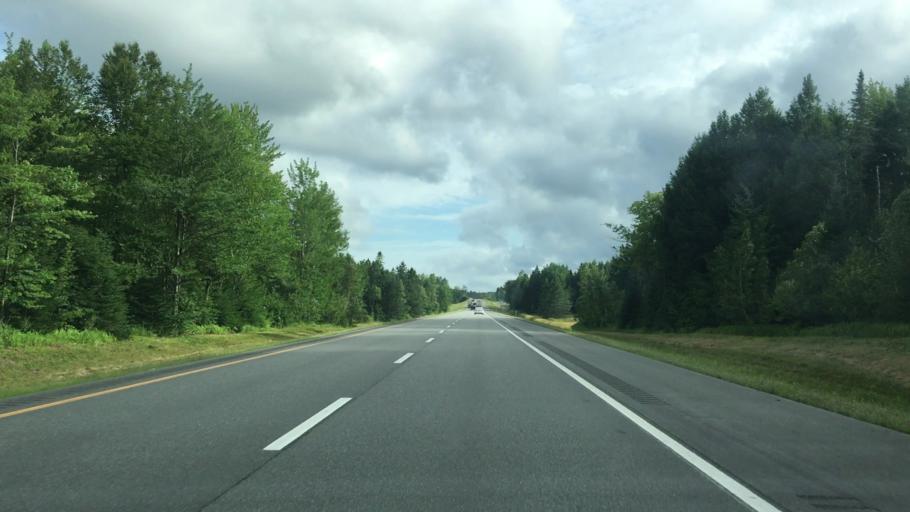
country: US
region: Maine
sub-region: Somerset County
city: Pittsfield
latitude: 44.7776
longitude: -69.4080
